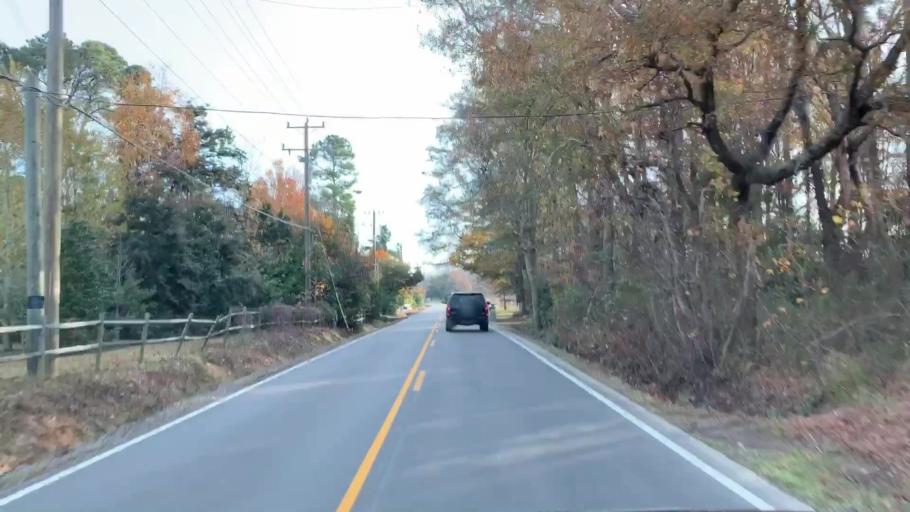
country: US
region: Virginia
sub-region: City of Virginia Beach
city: Virginia Beach
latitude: 36.6907
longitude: -76.0287
